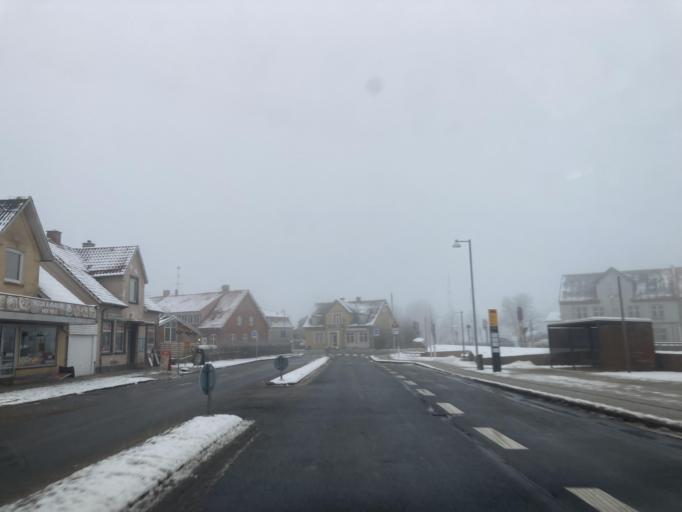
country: DK
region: Zealand
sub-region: Soro Kommune
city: Stenlille
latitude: 55.5390
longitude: 11.5909
